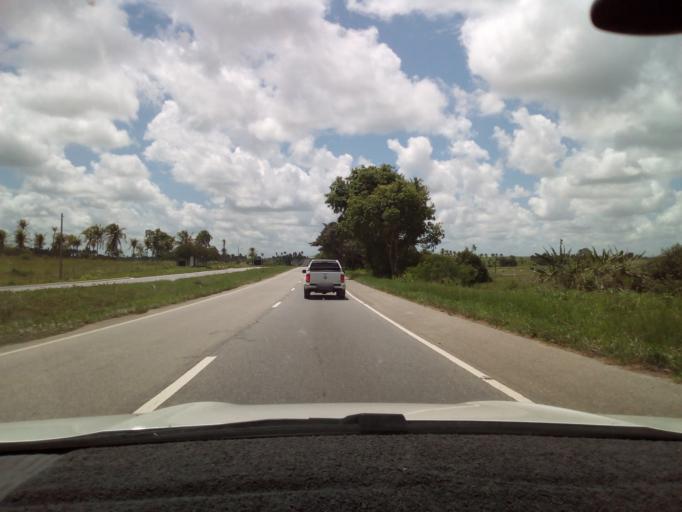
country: BR
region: Paraiba
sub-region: Pilar
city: Pilar
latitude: -7.1901
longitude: -35.2524
